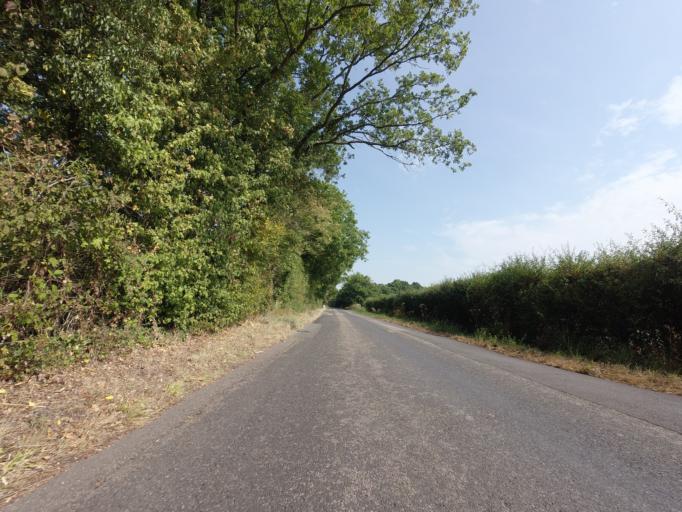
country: GB
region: England
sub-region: Kent
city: Headcorn
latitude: 51.1533
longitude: 0.6044
